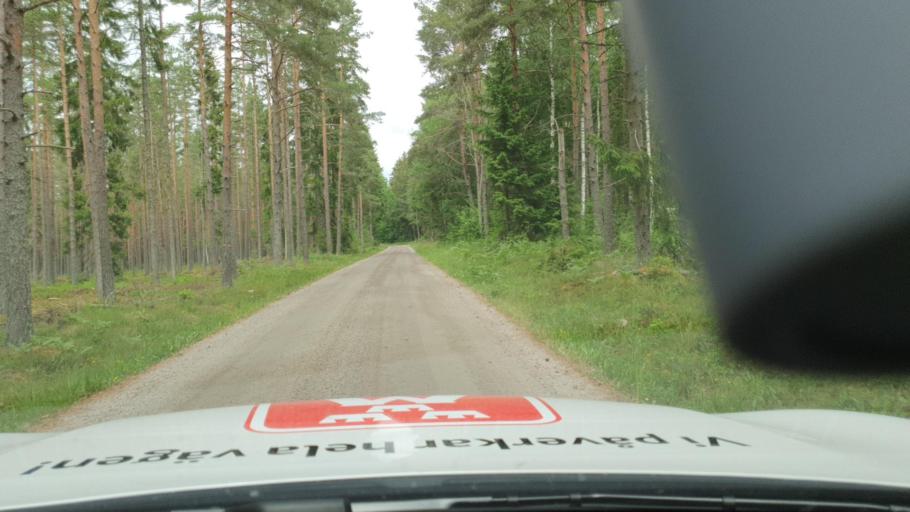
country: SE
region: Vaestra Goetaland
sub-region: Tidaholms Kommun
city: Tidaholm
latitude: 58.1758
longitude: 14.0445
